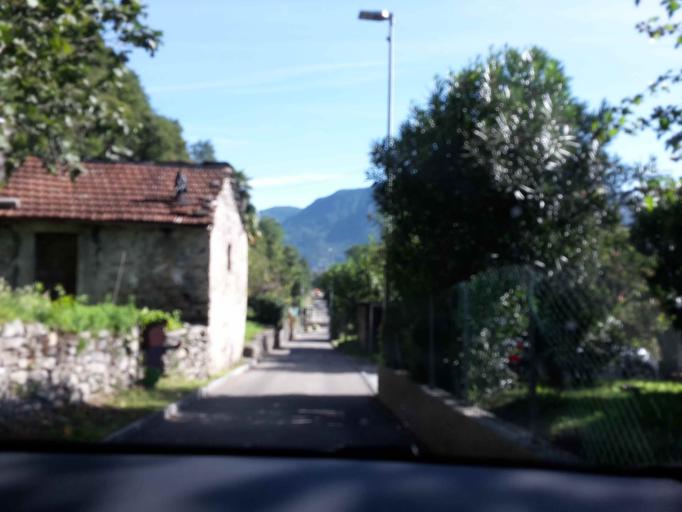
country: CH
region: Ticino
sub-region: Bellinzona District
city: Sementina
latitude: 46.1779
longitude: 8.9697
